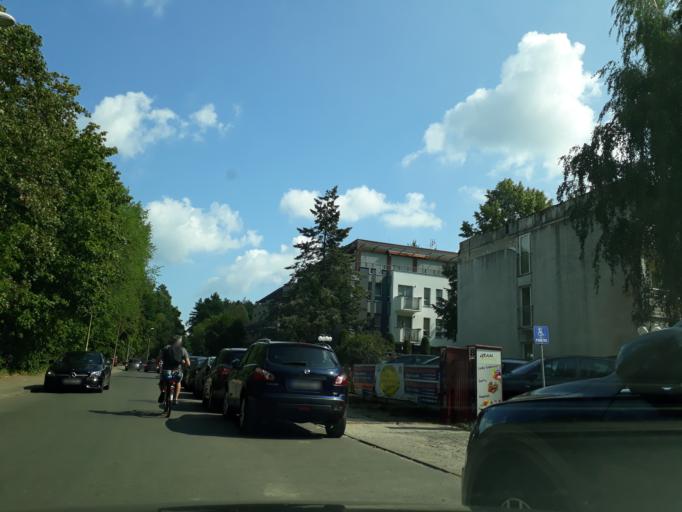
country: PL
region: West Pomeranian Voivodeship
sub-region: Swinoujscie
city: Swinoujscie
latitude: 53.9214
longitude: 14.2241
